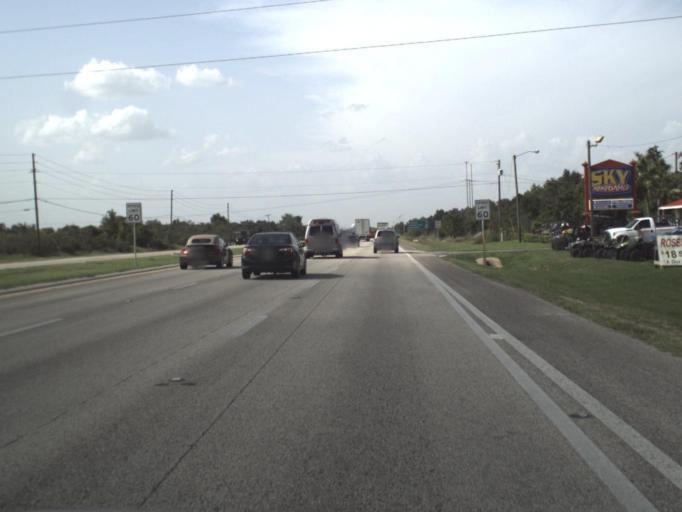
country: US
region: Florida
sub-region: Polk County
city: Lake Wales
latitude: 27.9161
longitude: -81.6039
